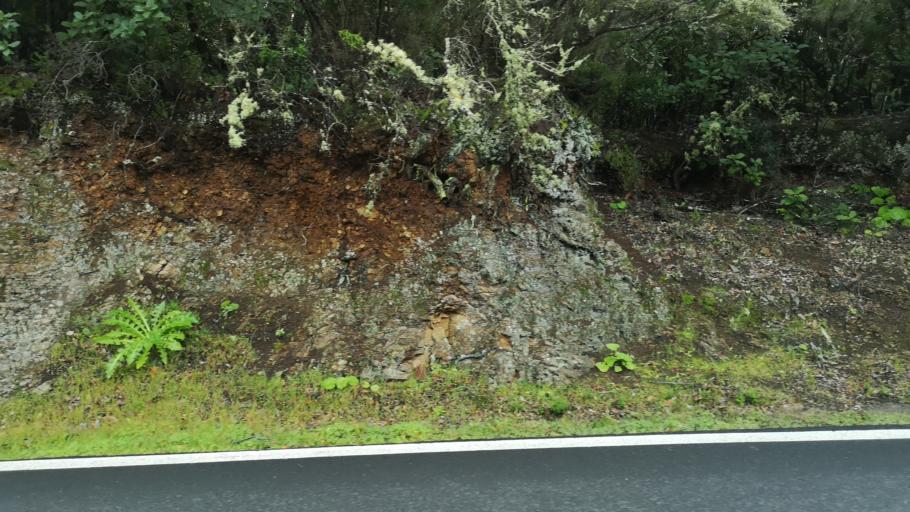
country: ES
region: Canary Islands
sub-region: Provincia de Santa Cruz de Tenerife
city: Vallehermosa
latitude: 28.1510
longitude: -17.3066
